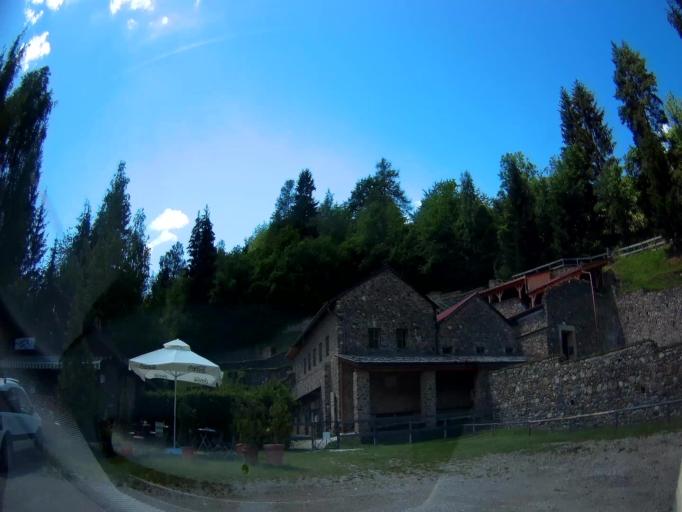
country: AT
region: Carinthia
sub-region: Politischer Bezirk Sankt Veit an der Glan
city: St. Georgen am Laengsee
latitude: 46.7245
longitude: 14.4286
